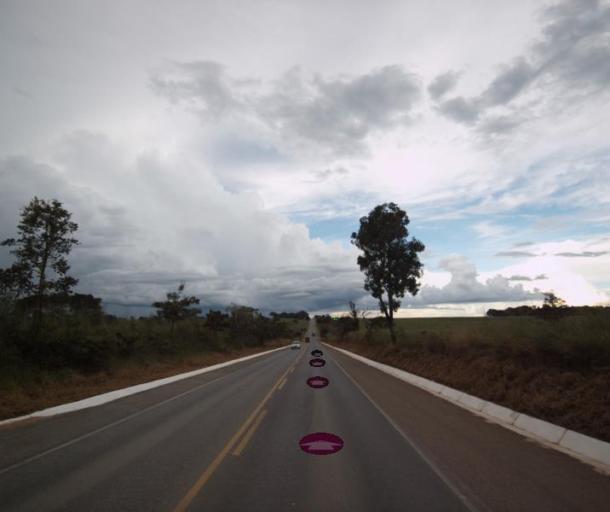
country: BR
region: Goias
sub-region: Itapaci
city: Itapaci
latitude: -14.9028
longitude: -49.3497
